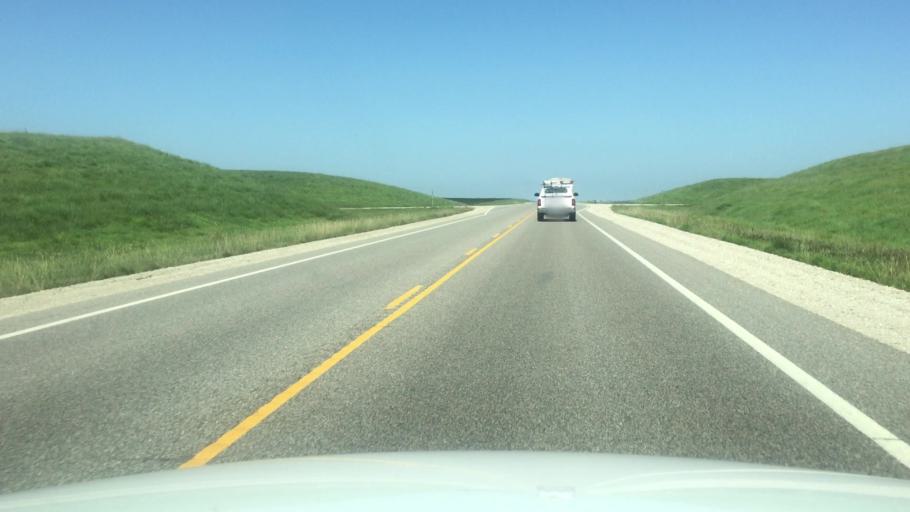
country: US
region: Kansas
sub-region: Doniphan County
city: Troy
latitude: 39.8002
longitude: -95.1700
